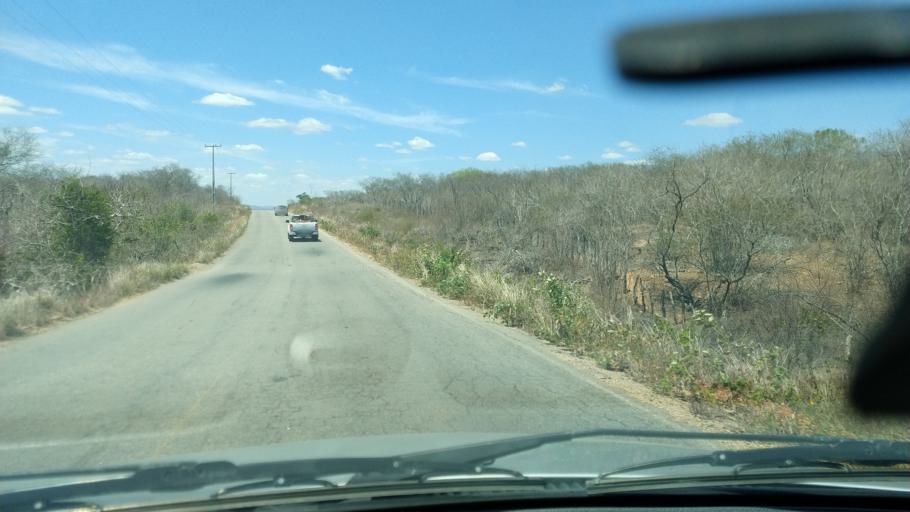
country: BR
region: Rio Grande do Norte
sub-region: Sao Paulo Do Potengi
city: Sao Paulo do Potengi
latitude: -5.9115
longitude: -35.5944
